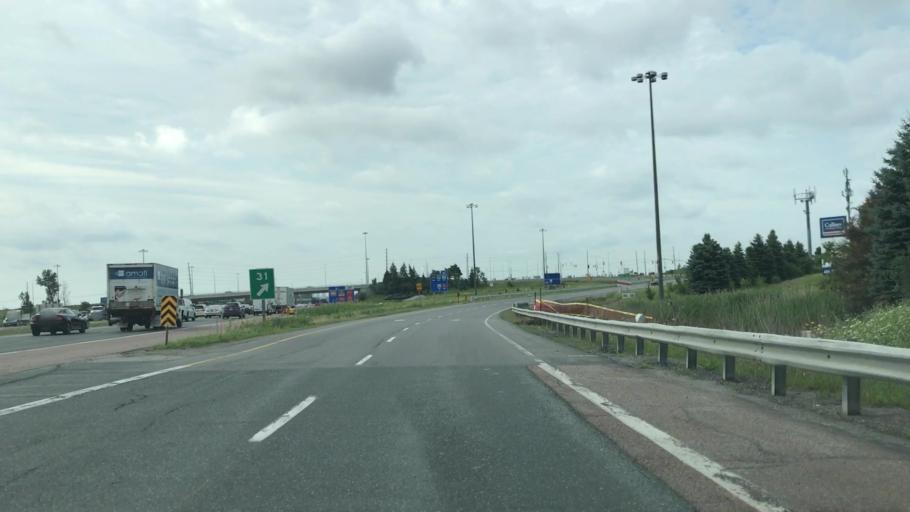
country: CA
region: Ontario
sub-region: York
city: Richmond Hill
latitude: 43.8866
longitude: -79.3811
